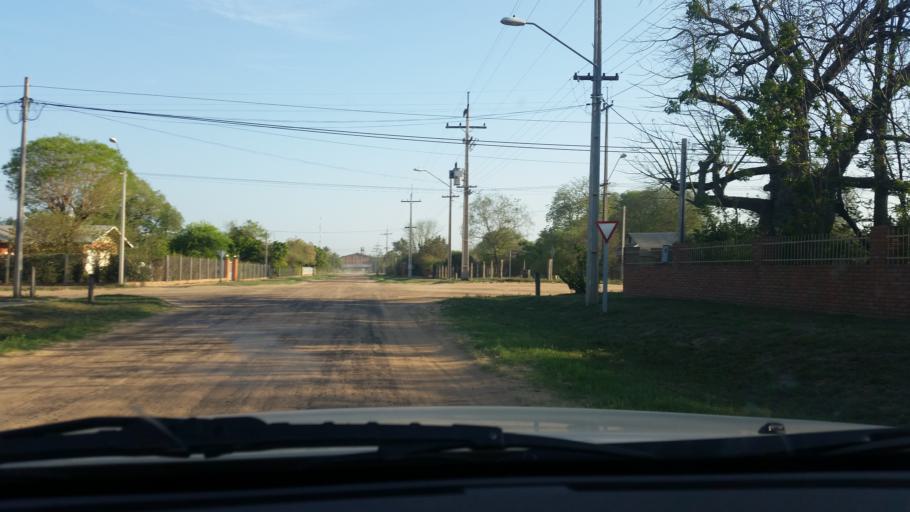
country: PY
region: Boqueron
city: Filadelfia
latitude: -22.3480
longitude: -60.0388
